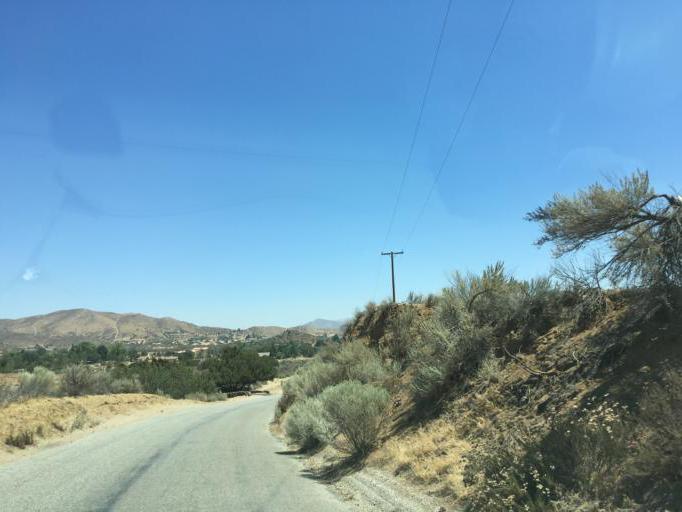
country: US
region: California
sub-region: Los Angeles County
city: Acton
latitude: 34.4734
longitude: -118.2042
